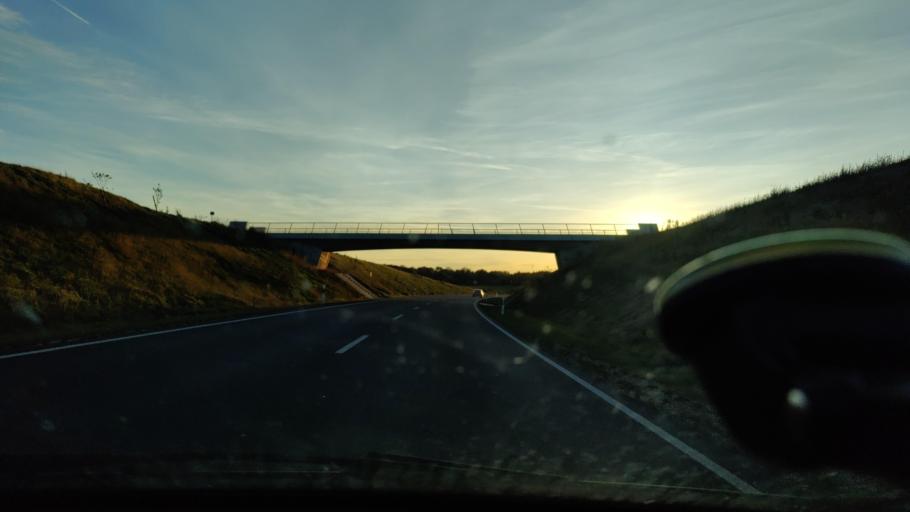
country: DE
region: North Rhine-Westphalia
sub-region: Regierungsbezirk Koln
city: Wassenberg
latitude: 51.0901
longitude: 6.1930
